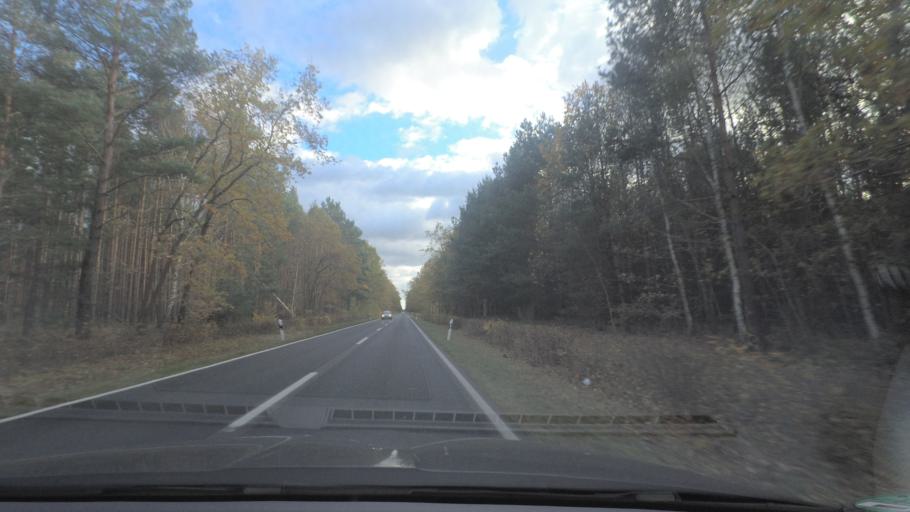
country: DE
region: Brandenburg
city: Sperenberg
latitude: 52.1231
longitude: 13.3678
